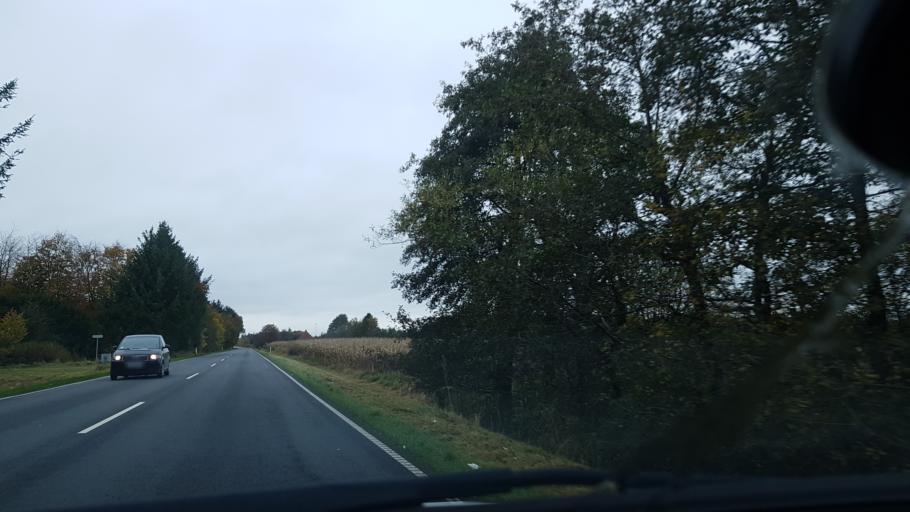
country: DK
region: South Denmark
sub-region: Esbjerg Kommune
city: Ribe
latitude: 55.2966
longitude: 8.8137
